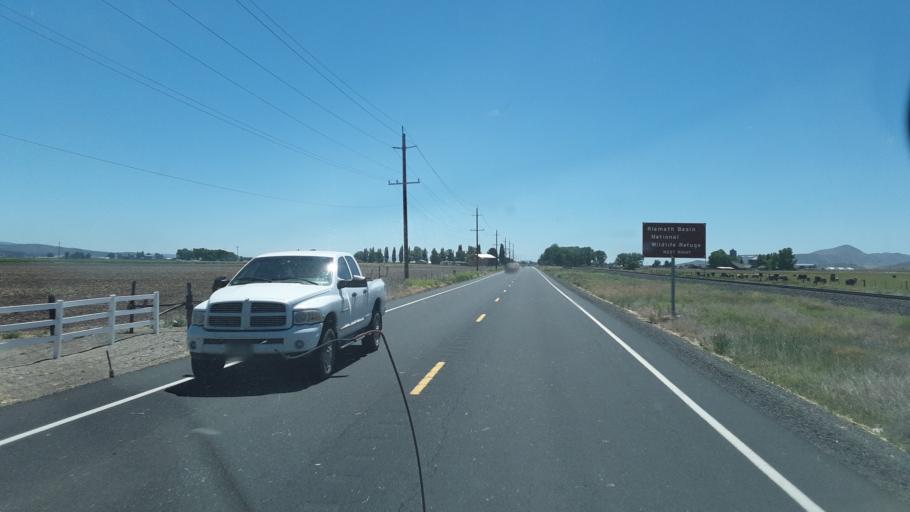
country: US
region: California
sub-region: Siskiyou County
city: Tulelake
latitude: 42.0487
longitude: -121.6352
